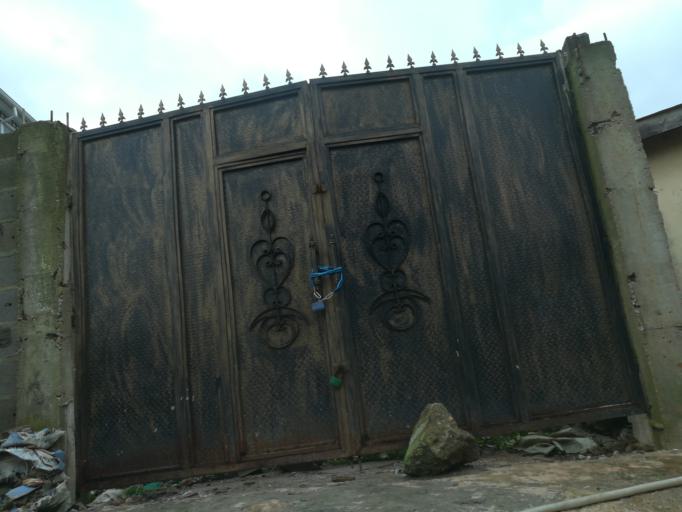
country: NG
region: Lagos
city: Agege
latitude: 6.6092
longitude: 3.3207
